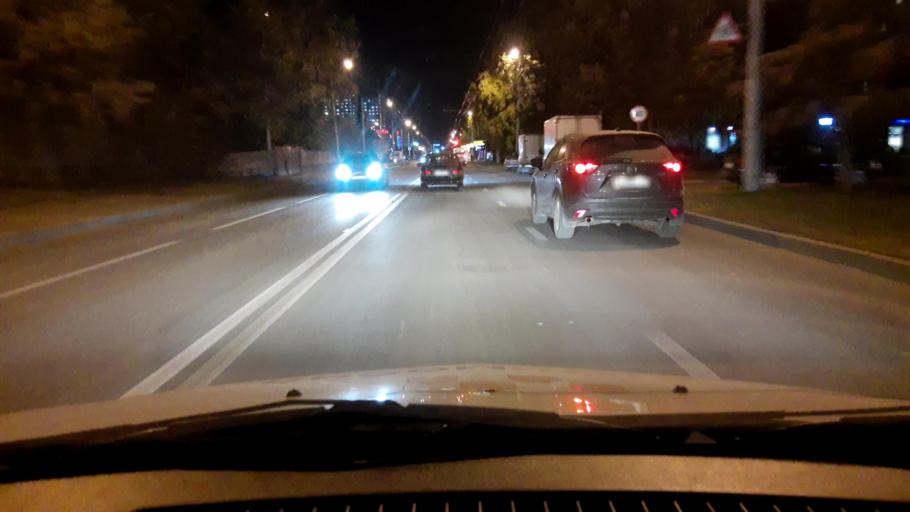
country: RU
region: Bashkortostan
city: Ufa
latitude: 54.7836
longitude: 56.1312
